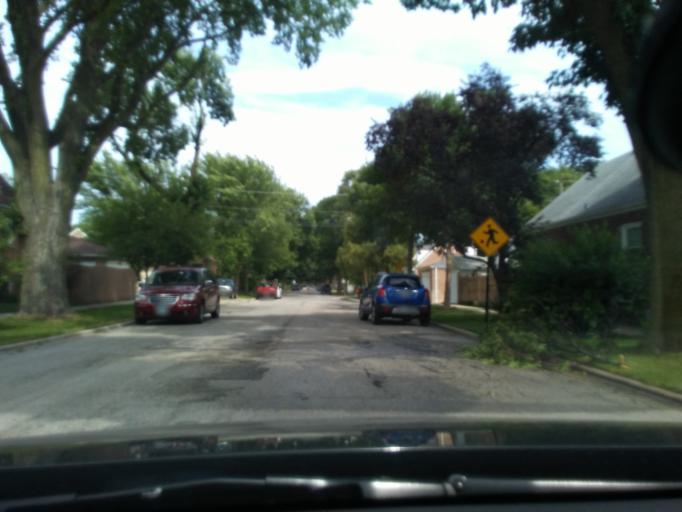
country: US
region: Illinois
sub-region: Cook County
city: Harwood Heights
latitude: 41.9738
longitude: -87.8000
